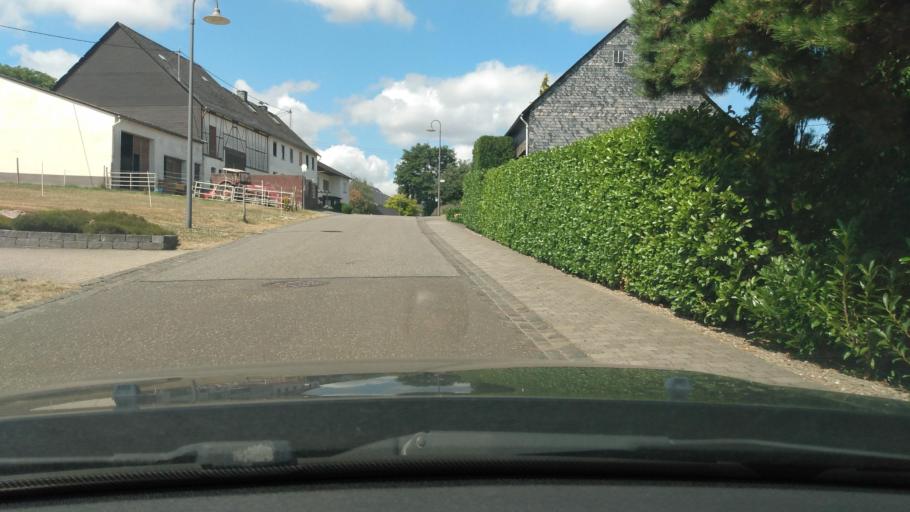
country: DE
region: Rheinland-Pfalz
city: Kleinich
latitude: 49.8842
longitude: 7.1737
